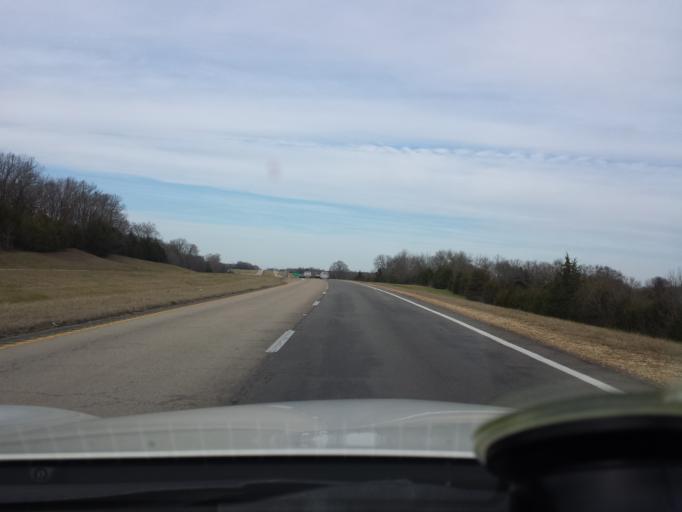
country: US
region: Mississippi
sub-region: Chickasaw County
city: Okolona
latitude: 33.9894
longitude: -88.7015
